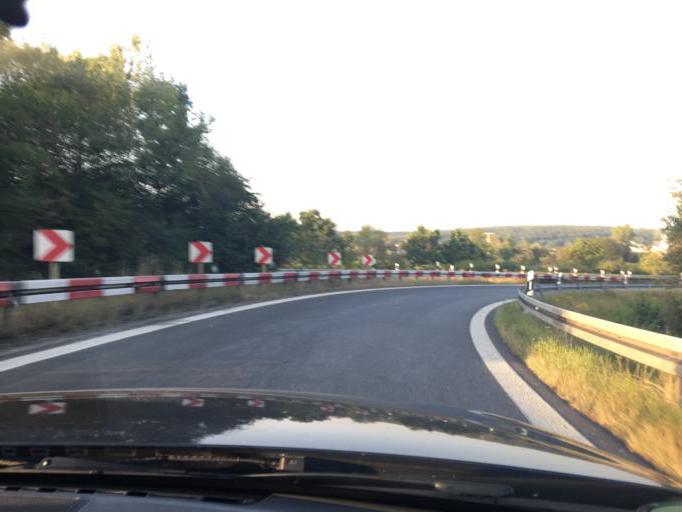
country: DE
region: Bavaria
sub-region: Upper Franconia
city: Gundelsheim
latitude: 49.9303
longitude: 10.9158
